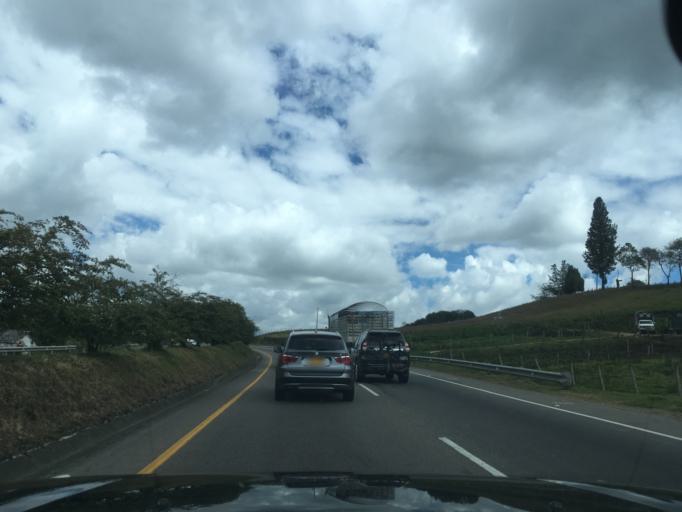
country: CO
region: Boyaca
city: Ventaquemada
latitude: 5.3436
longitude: -73.5527
